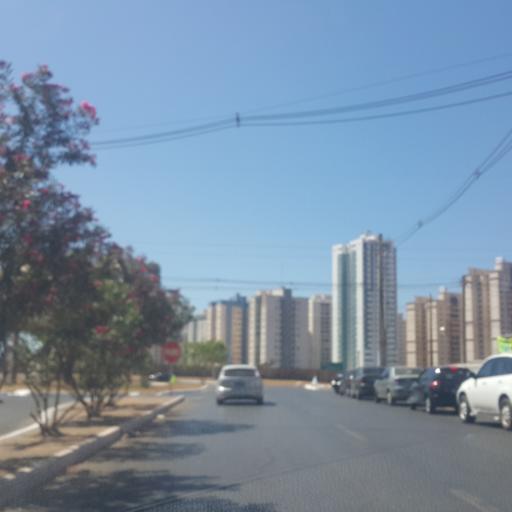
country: BR
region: Federal District
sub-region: Brasilia
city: Brasilia
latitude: -15.8419
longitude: -48.0428
